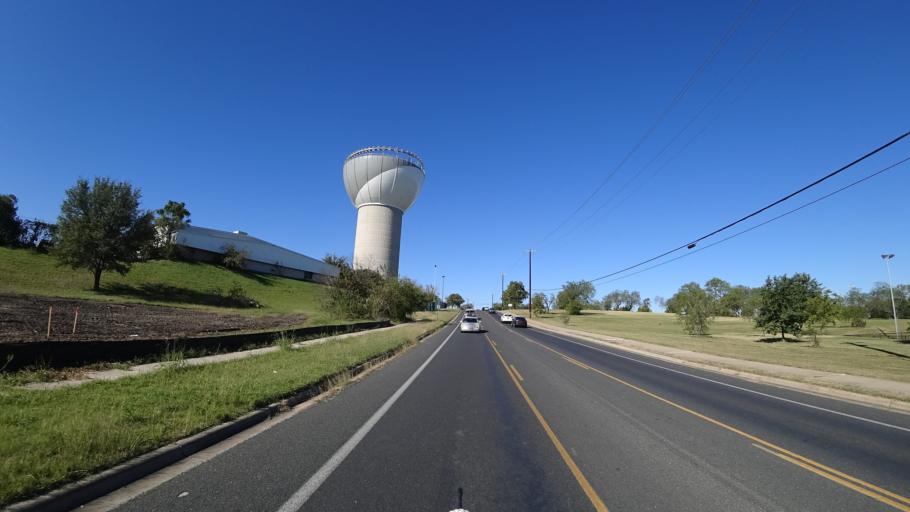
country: US
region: Texas
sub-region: Travis County
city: Austin
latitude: 30.3014
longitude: -97.6922
